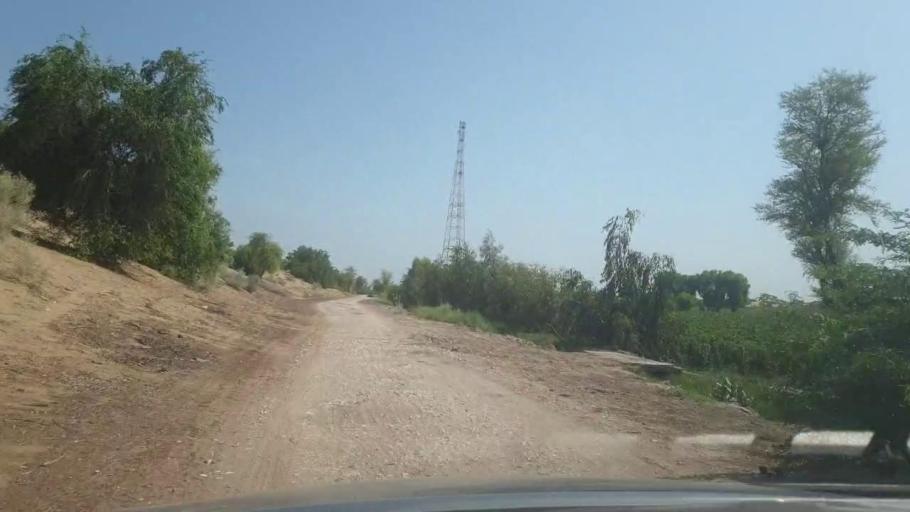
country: PK
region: Sindh
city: Khairpur
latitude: 27.3997
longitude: 69.0796
